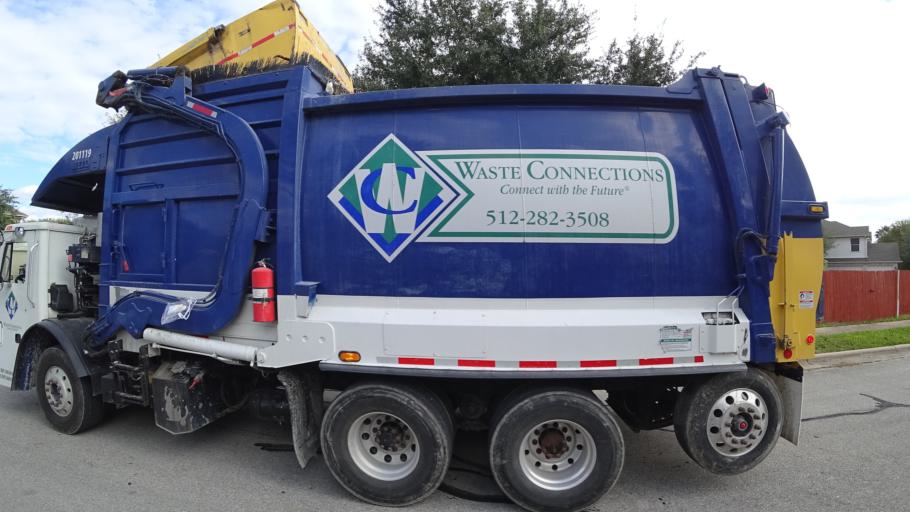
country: US
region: Texas
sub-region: Travis County
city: Pflugerville
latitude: 30.4296
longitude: -97.6261
